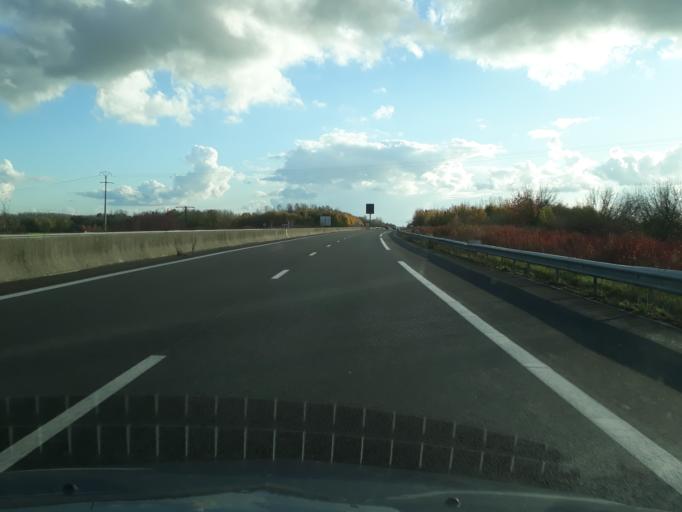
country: FR
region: Champagne-Ardenne
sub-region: Departement de la Marne
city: Fagnieres
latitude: 49.0033
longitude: 4.2985
